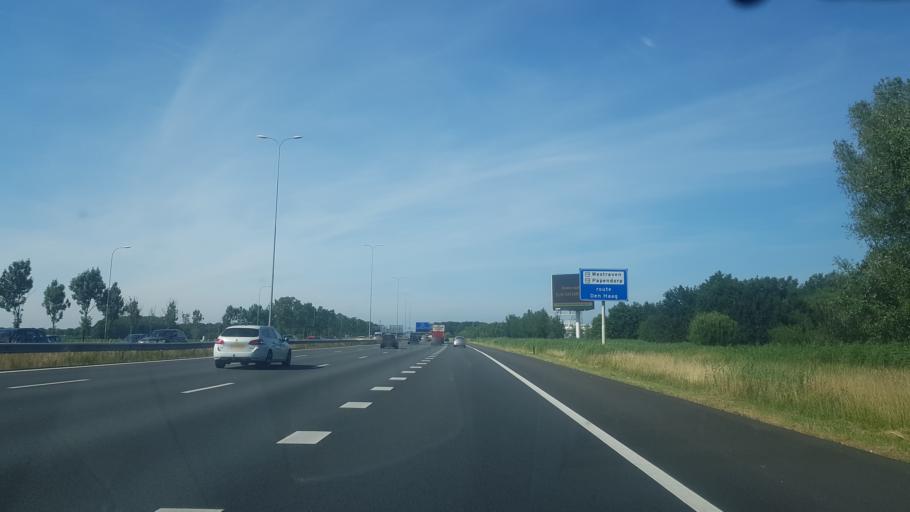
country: NL
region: Utrecht
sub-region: Gemeente Utrecht
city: Lunetten
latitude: 52.0362
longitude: 5.1386
